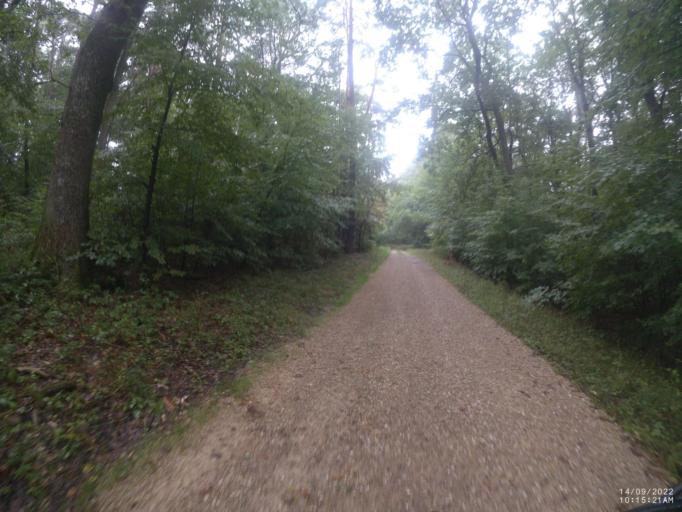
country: DE
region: Rheinland-Pfalz
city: Uxheim
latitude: 50.3359
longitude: 6.7269
